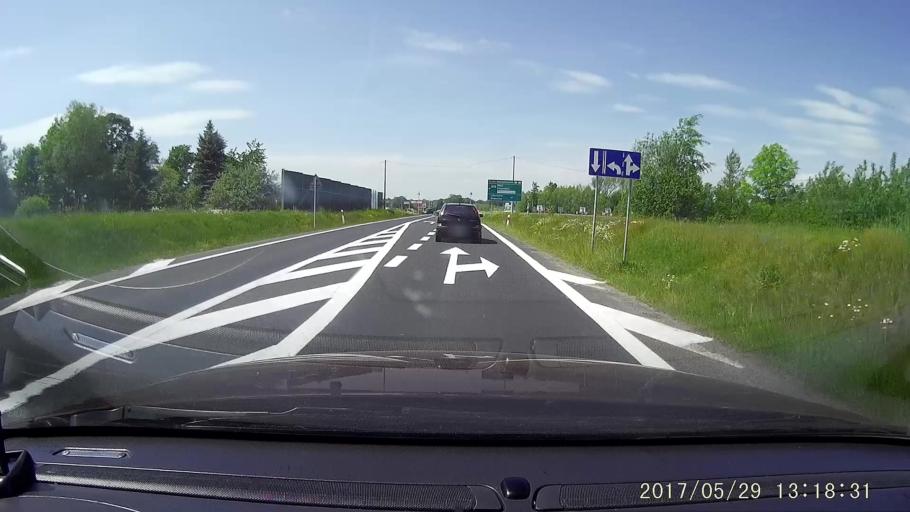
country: PL
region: Lower Silesian Voivodeship
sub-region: Powiat lwowecki
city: Gryfow Slaski
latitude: 51.0078
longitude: 15.4474
